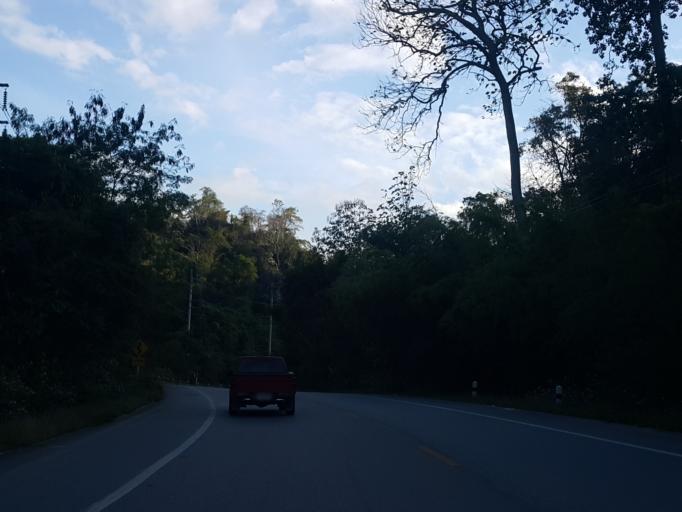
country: TH
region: Lampang
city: Lampang
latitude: 18.4898
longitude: 99.5473
